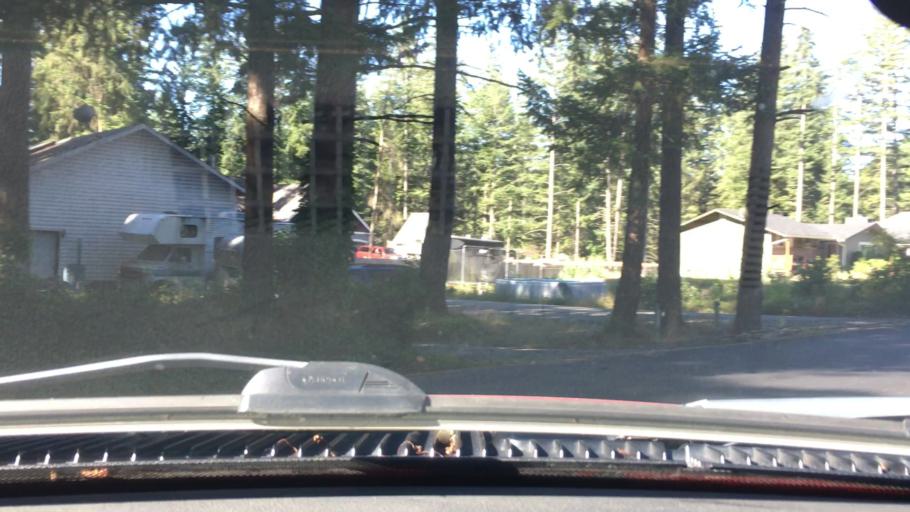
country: US
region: Washington
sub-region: King County
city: Lake Morton-Berrydale
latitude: 47.3175
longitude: -122.0995
